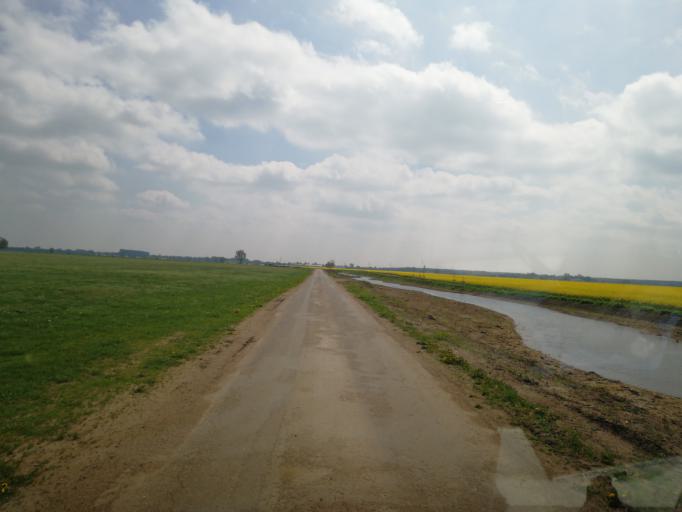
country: DE
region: Brandenburg
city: Doberlug-Kirchhain
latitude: 51.6733
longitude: 13.5370
